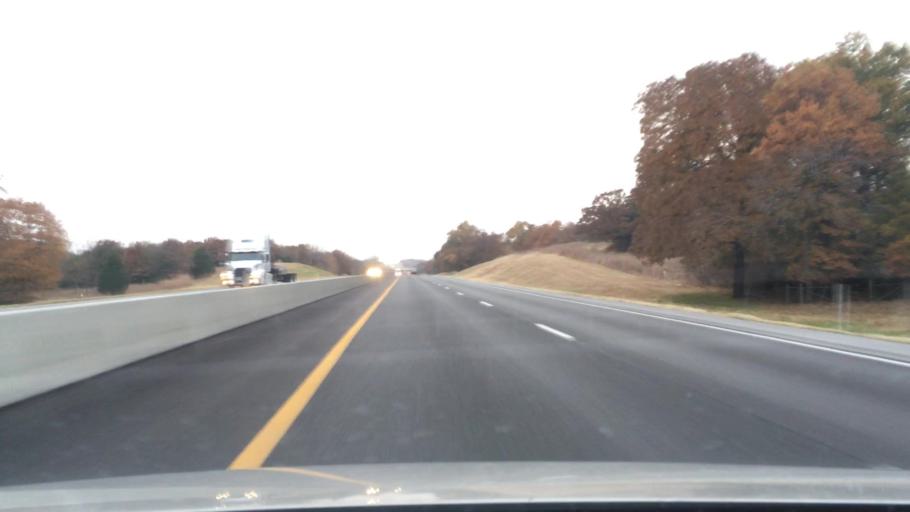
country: US
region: Oklahoma
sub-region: Lincoln County
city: Stroud
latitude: 35.7423
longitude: -96.7509
